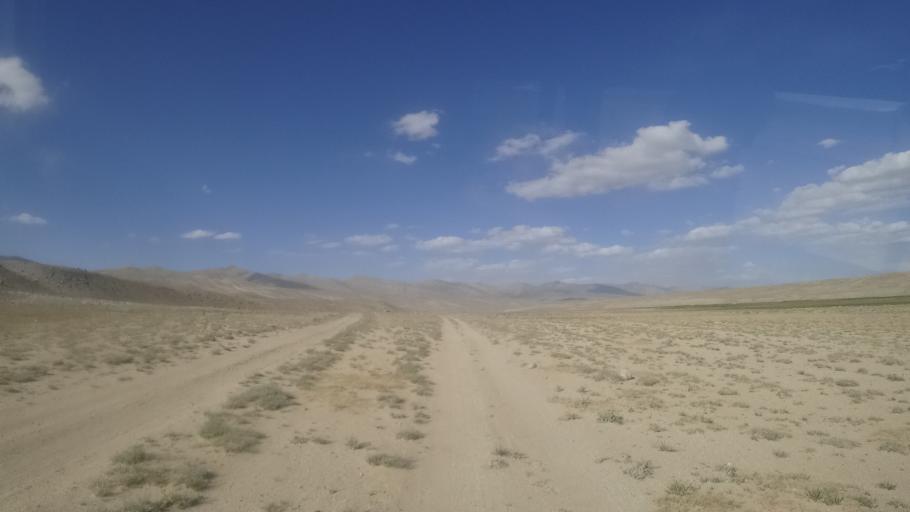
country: AF
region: Badakhshan
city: Khandud
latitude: 37.4219
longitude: 73.2368
